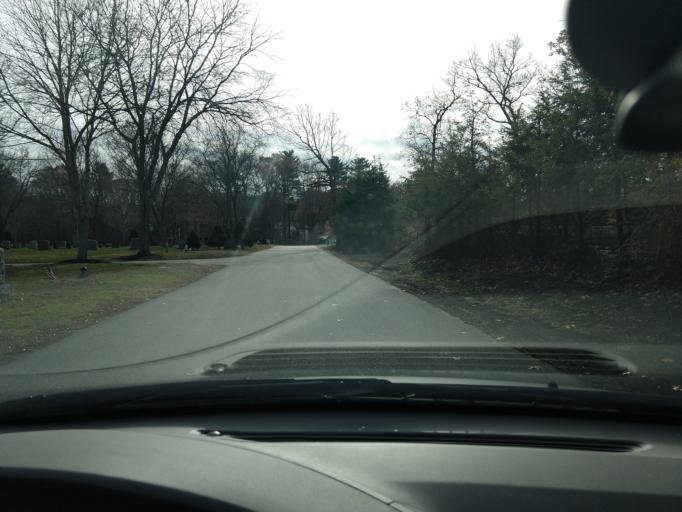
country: US
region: Massachusetts
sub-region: Middlesex County
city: Bedford
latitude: 42.4871
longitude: -71.2544
